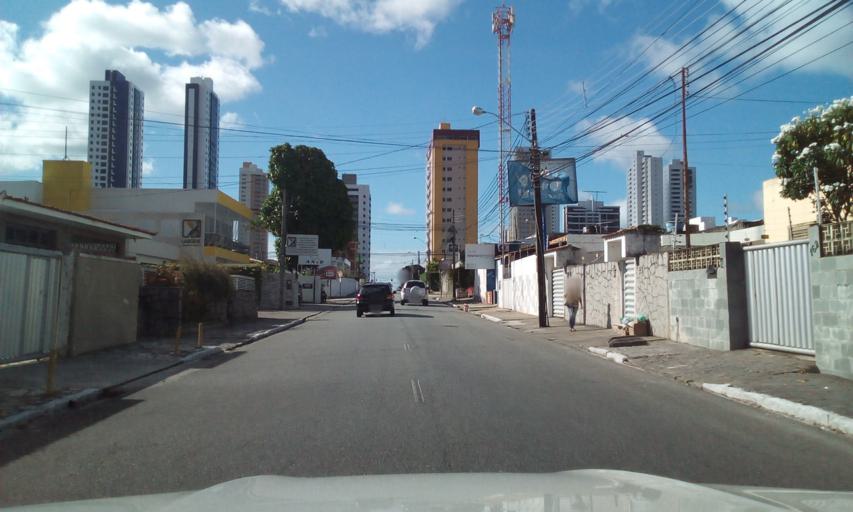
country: BR
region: Paraiba
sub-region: Joao Pessoa
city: Joao Pessoa
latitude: -7.1183
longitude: -34.8533
